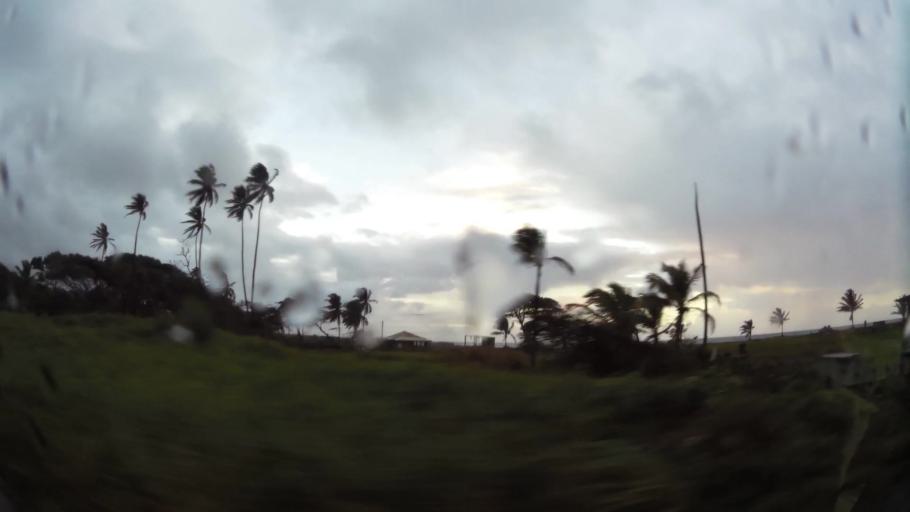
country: DM
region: Saint Andrew
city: Marigot
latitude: 15.5463
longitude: -61.2923
